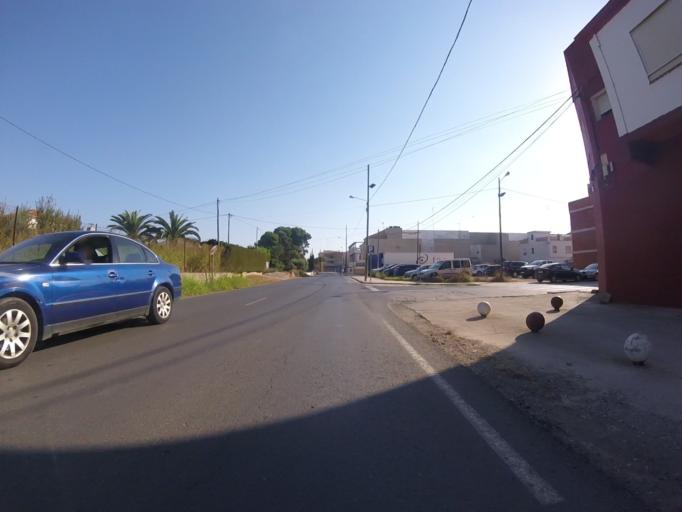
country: ES
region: Valencia
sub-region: Provincia de Castello
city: Benicarlo
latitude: 40.4118
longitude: 0.4215
